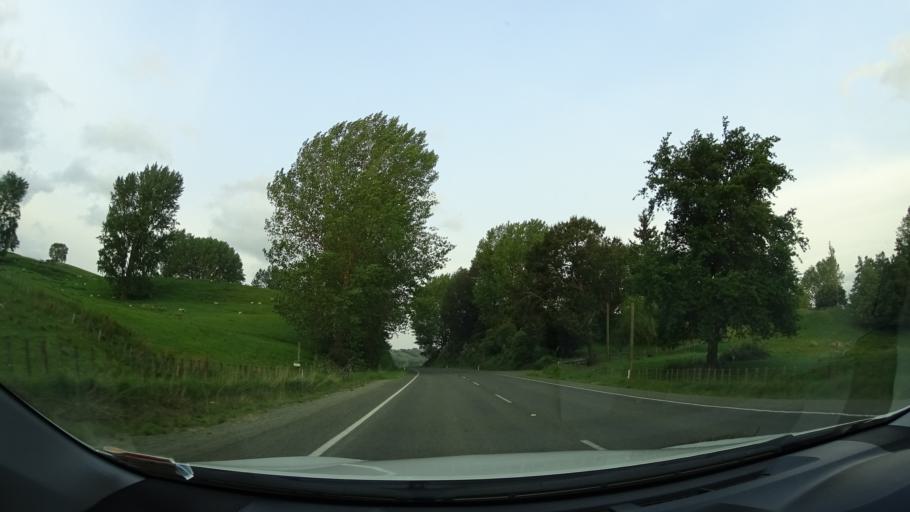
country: NZ
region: Manawatu-Wanganui
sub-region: Ruapehu District
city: Waiouru
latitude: -39.7411
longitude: 175.8381
